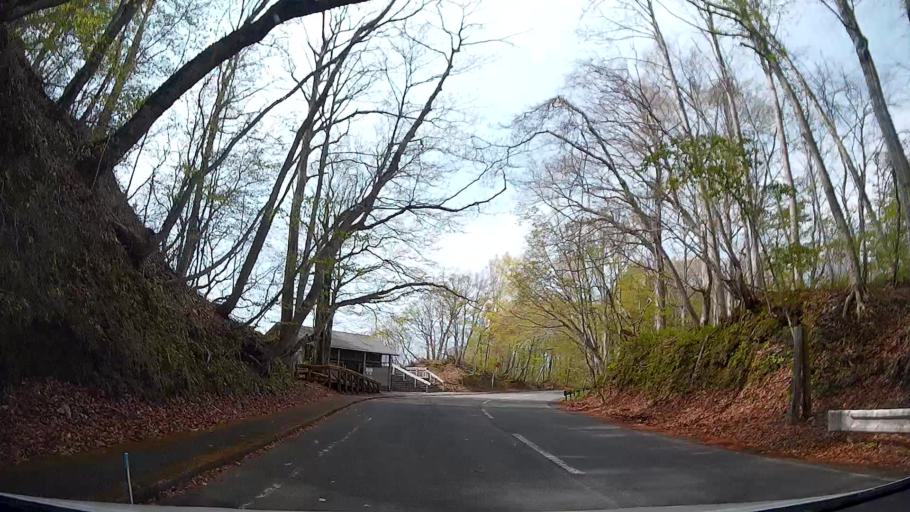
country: JP
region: Akita
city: Hanawa
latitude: 40.4402
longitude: 140.9180
